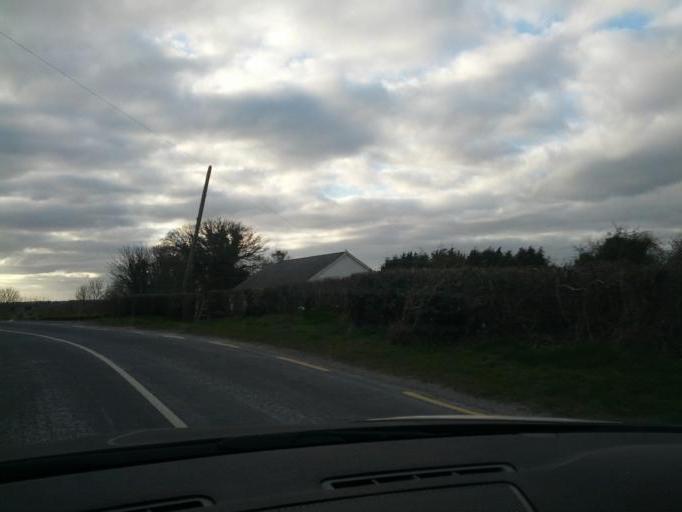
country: IE
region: Leinster
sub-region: An Iarmhi
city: Athlone
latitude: 53.3232
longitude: -7.9310
